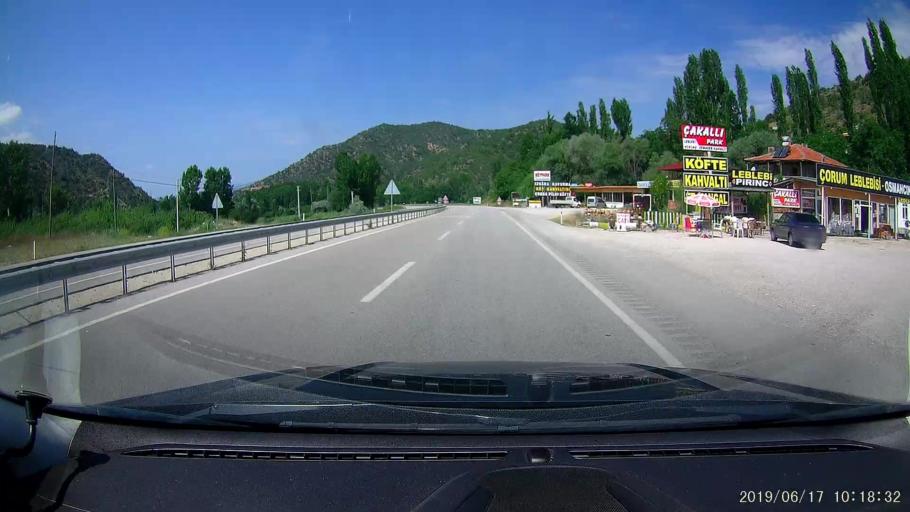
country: TR
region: Corum
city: Osmancik
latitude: 40.9786
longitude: 34.9196
